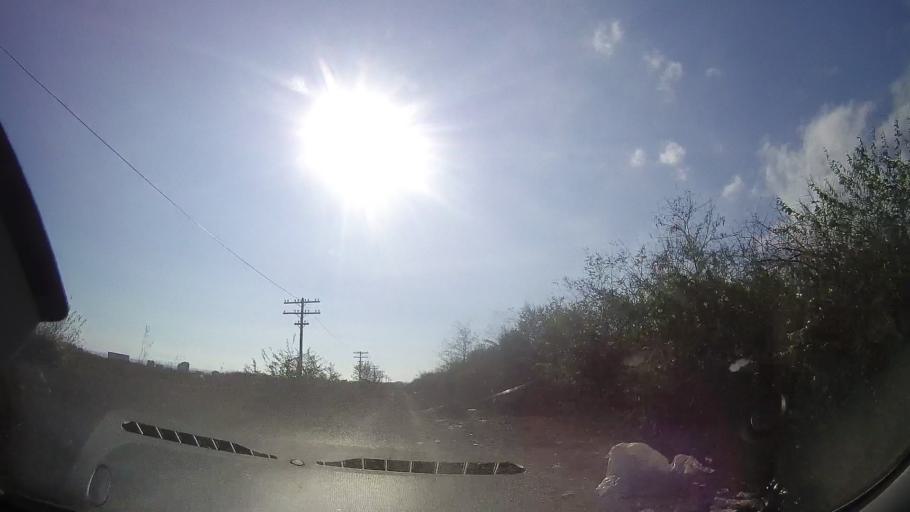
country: RO
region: Constanta
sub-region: Comuna Costinesti
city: Costinesti
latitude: 43.9720
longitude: 28.6433
